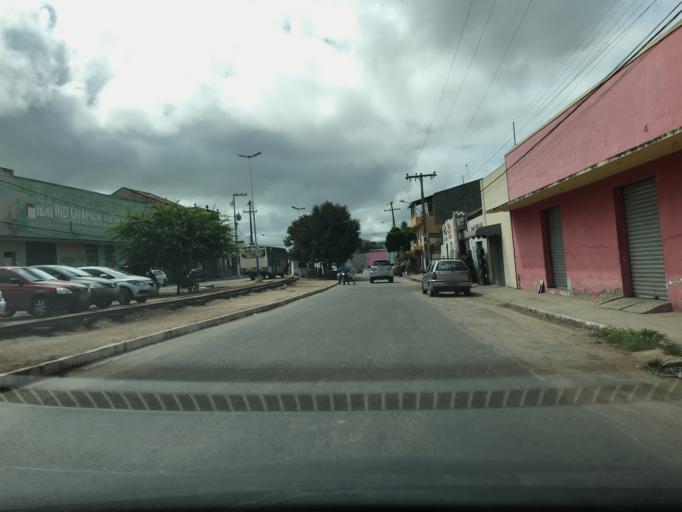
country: BR
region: Pernambuco
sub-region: Bezerros
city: Bezerros
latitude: -8.2336
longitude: -35.7544
